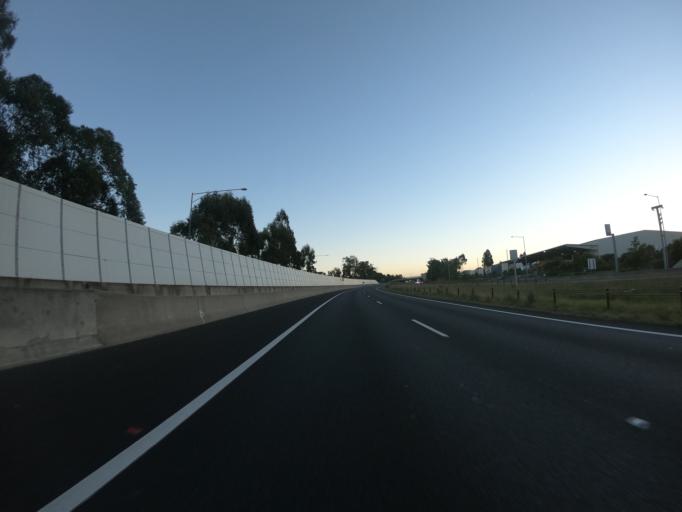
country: AU
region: New South Wales
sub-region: Blacktown
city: Glendenning
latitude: -33.7498
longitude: 150.8456
